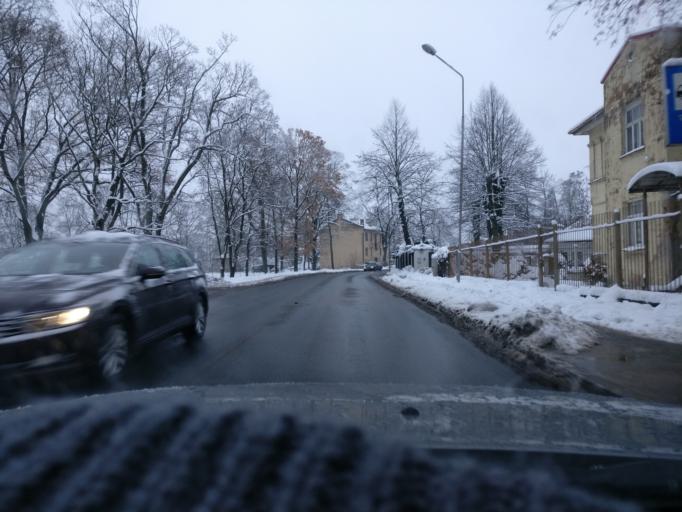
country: LV
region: Riga
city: Riga
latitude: 56.9283
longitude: 24.0806
